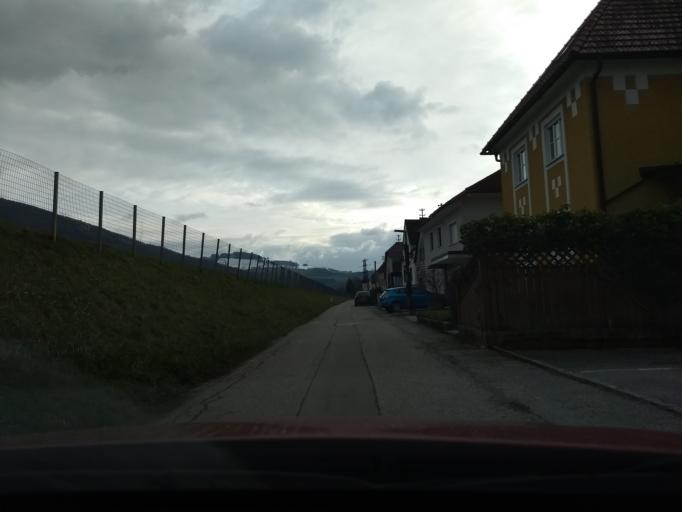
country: AT
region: Upper Austria
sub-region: Politischer Bezirk Steyr-Land
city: Garsten
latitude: 48.0152
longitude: 14.4087
